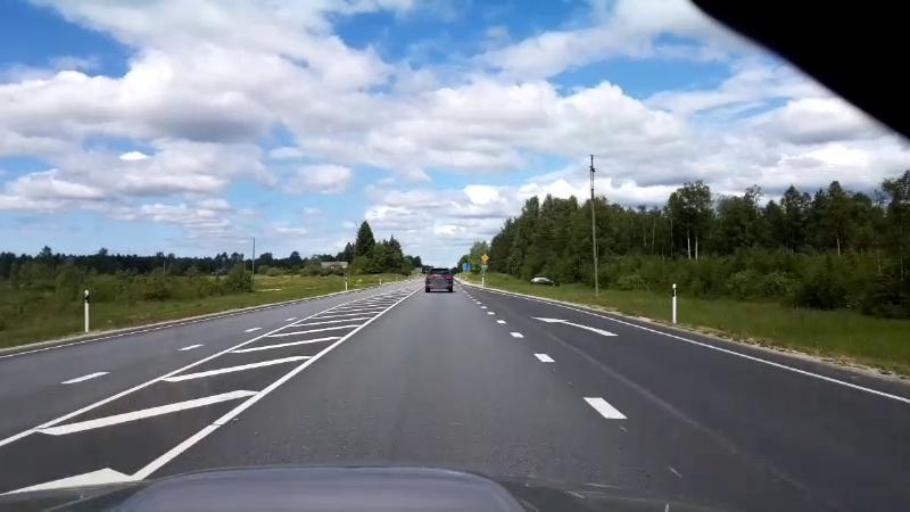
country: EE
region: Raplamaa
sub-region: Maerjamaa vald
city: Marjamaa
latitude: 59.0500
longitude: 24.4448
